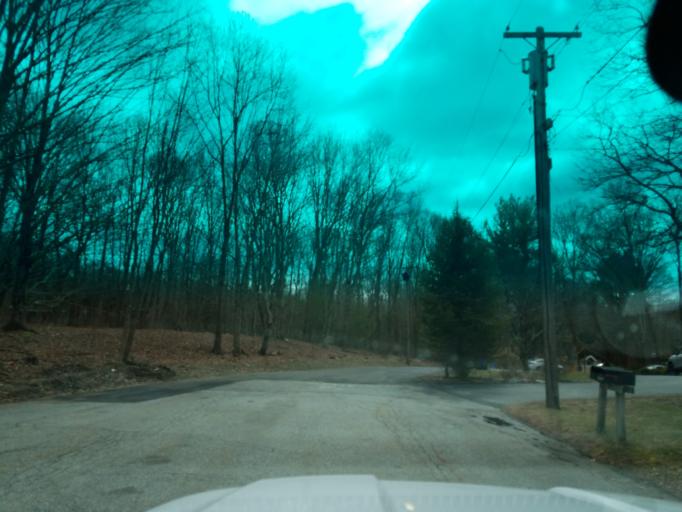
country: US
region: Connecticut
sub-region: Windham County
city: Danielson
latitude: 41.8143
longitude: -71.8748
